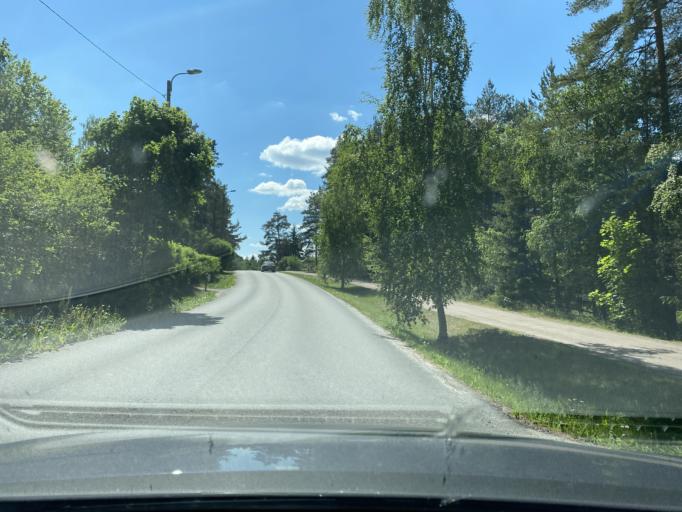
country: FI
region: Satakunta
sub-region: Rauma
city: Eura
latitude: 61.1270
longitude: 22.1629
